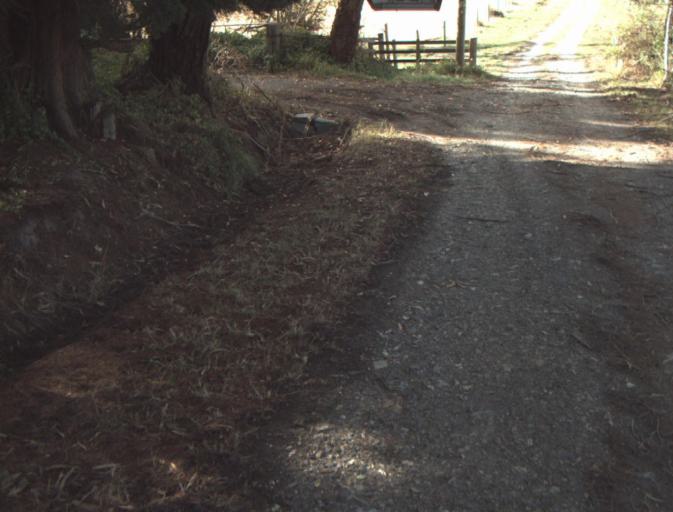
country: AU
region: Tasmania
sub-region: Launceston
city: Mayfield
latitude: -41.2375
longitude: 147.1626
